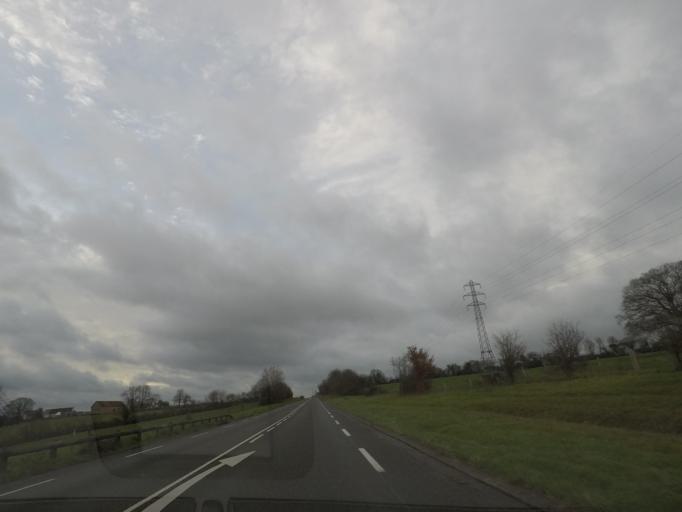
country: FR
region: Pays de la Loire
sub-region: Departement de la Sarthe
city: La Ferte-Bernard
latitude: 48.1830
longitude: 0.6214
